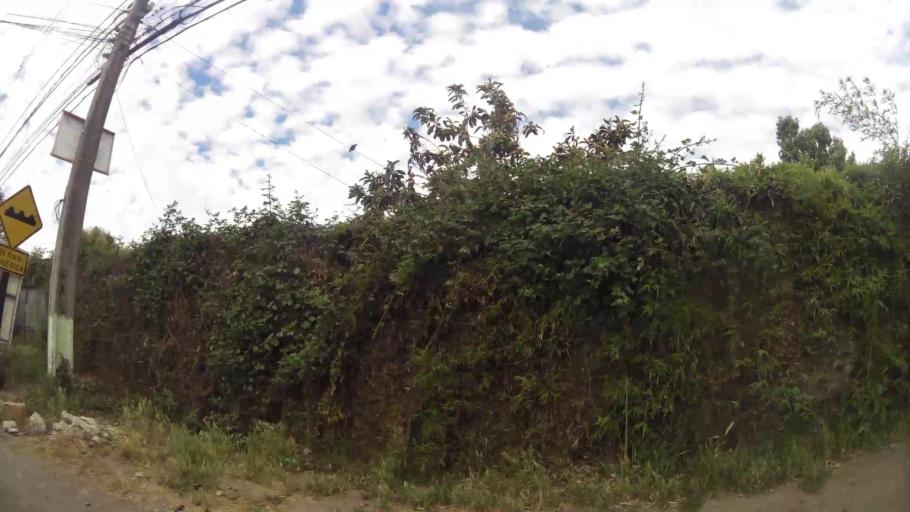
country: CL
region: Santiago Metropolitan
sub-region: Provincia de Santiago
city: La Pintana
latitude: -33.6204
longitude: -70.6240
